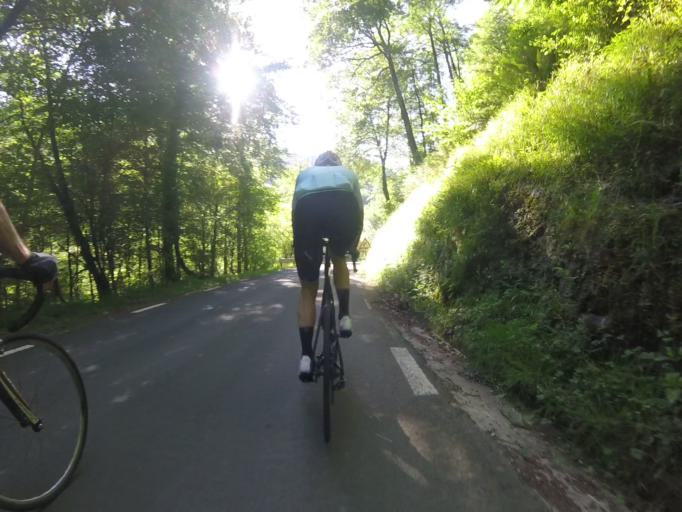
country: ES
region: Basque Country
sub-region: Provincia de Guipuzcoa
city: Beizama
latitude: 43.1388
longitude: -2.2186
